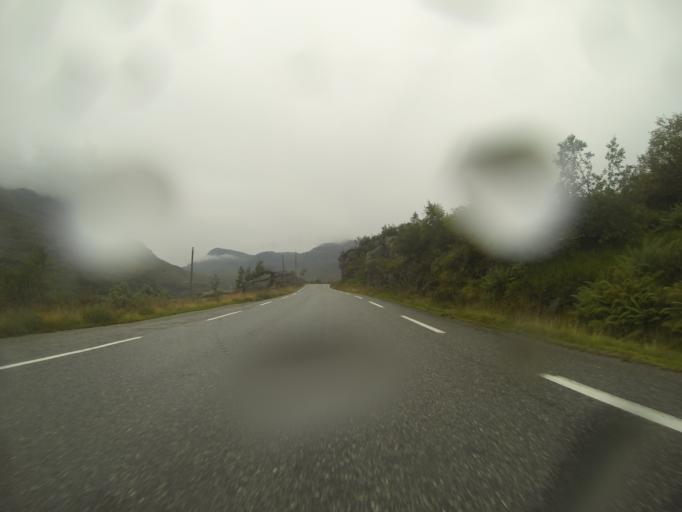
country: NO
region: Rogaland
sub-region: Sauda
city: Sauda
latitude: 59.7277
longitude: 6.5845
